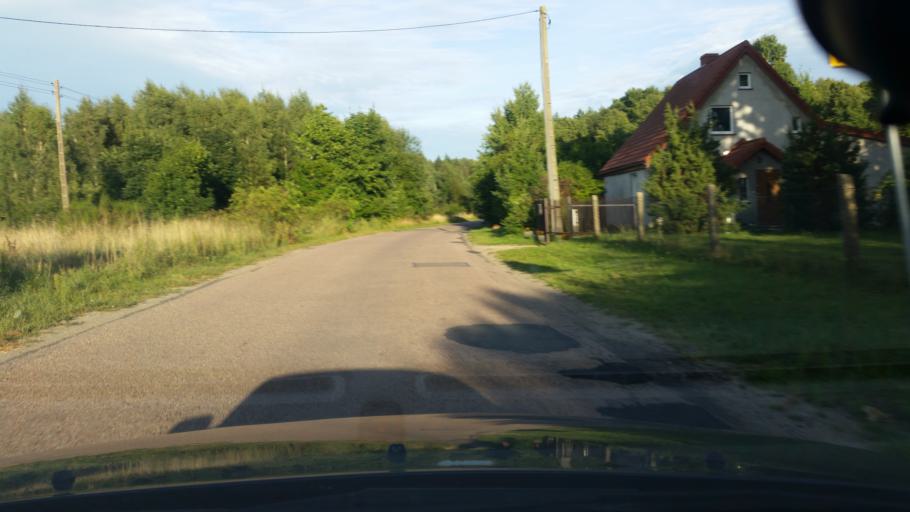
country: PL
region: Pomeranian Voivodeship
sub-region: Powiat wejherowski
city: Choczewo
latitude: 54.7631
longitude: 17.7668
